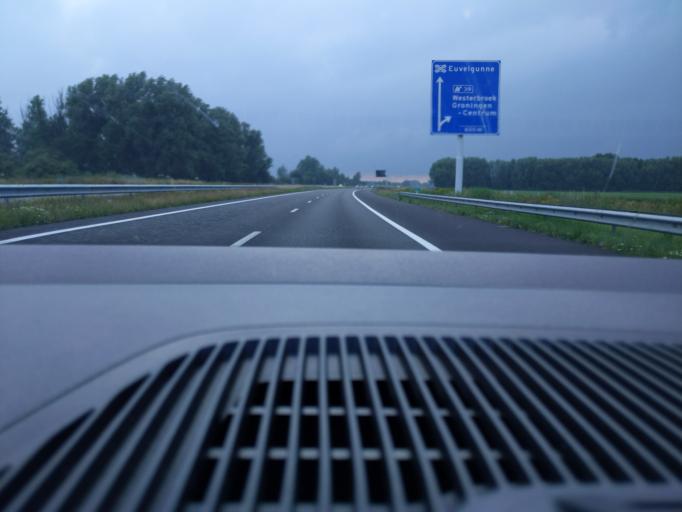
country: NL
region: Groningen
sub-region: Gemeente Haren
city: Haren
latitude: 53.1999
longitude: 6.6456
